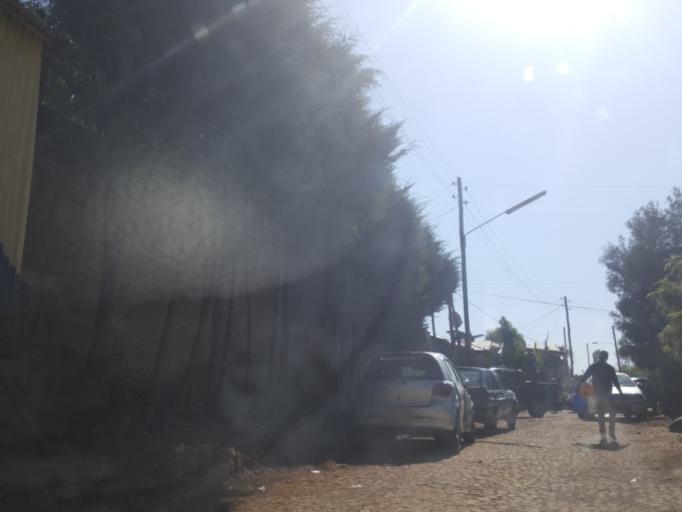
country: ET
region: Adis Abeba
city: Addis Ababa
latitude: 9.0489
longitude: 38.7340
